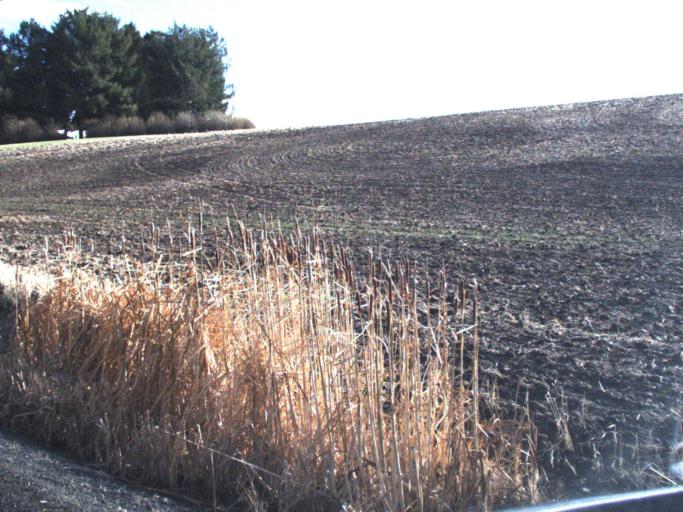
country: US
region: Washington
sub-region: Whitman County
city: Colfax
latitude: 46.9395
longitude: -117.1643
